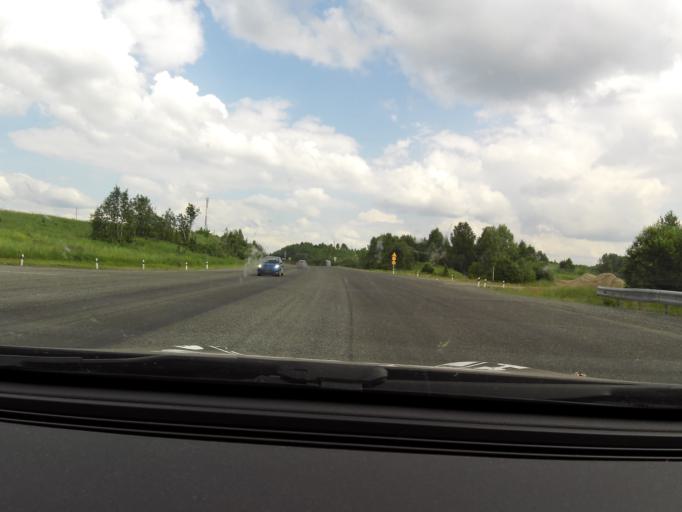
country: RU
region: Sverdlovsk
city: Ufimskiy
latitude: 56.7871
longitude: 58.3628
